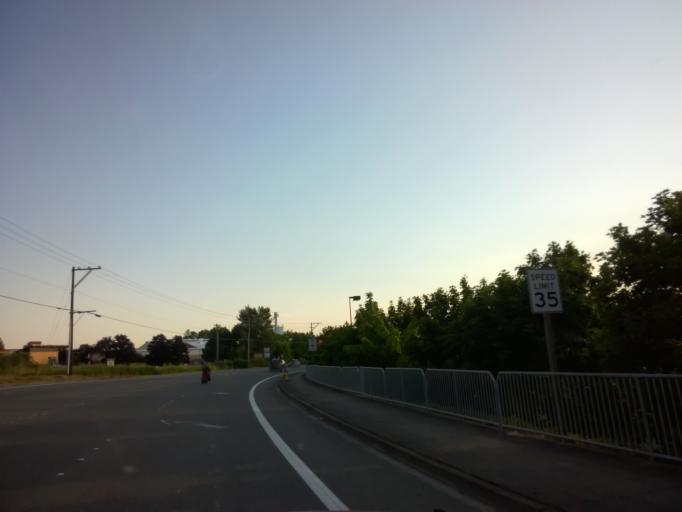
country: US
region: Washington
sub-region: King County
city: Woodinville
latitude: 47.7788
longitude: -122.1474
